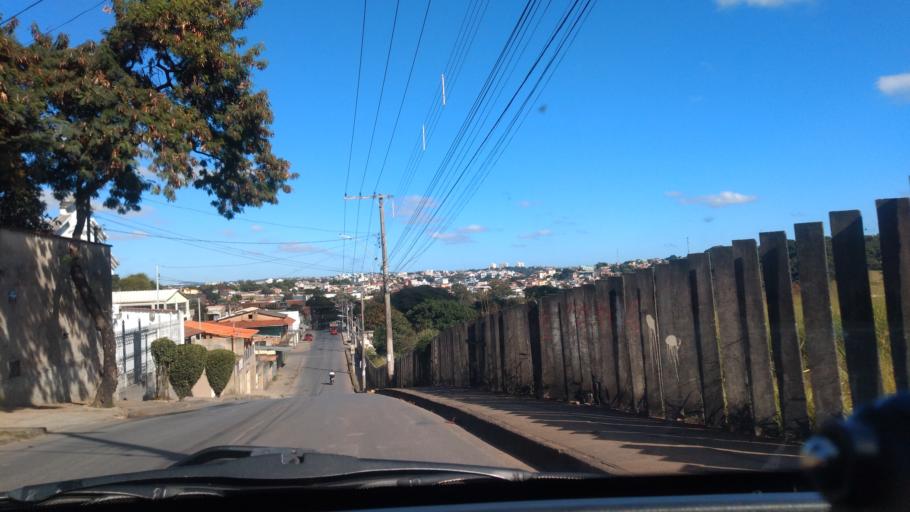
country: BR
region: Minas Gerais
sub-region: Santa Luzia
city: Santa Luzia
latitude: -19.8104
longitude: -43.9418
